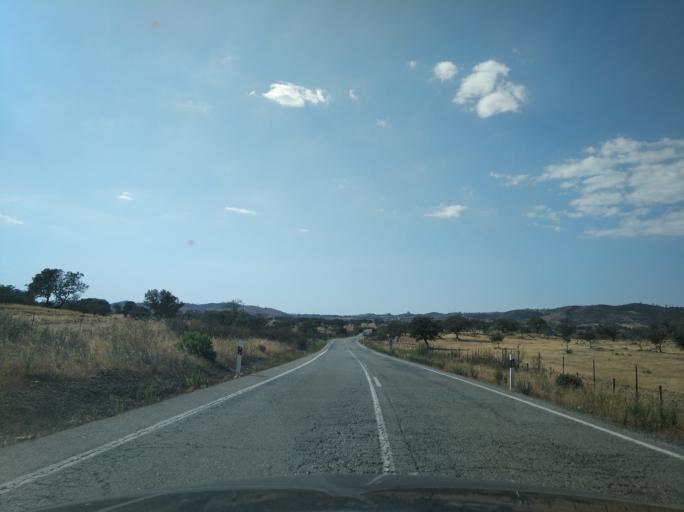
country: ES
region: Andalusia
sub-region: Provincia de Huelva
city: Santa Barbara de Casa
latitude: 37.7742
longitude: -7.1478
